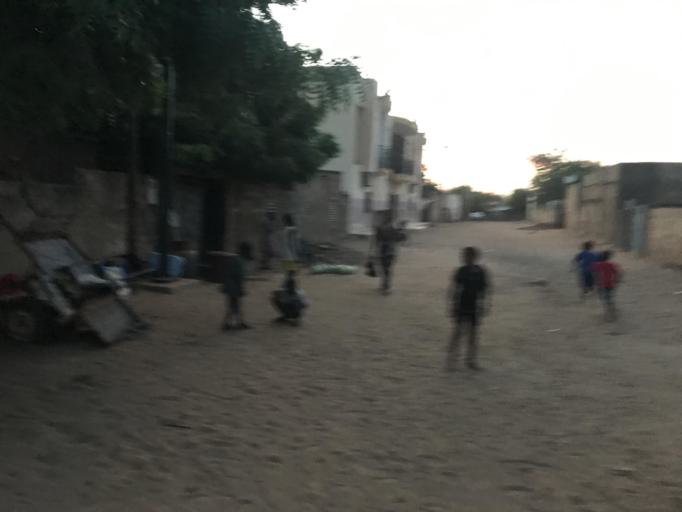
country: SN
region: Louga
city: Ndibene Dahra
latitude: 15.3946
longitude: -15.1195
